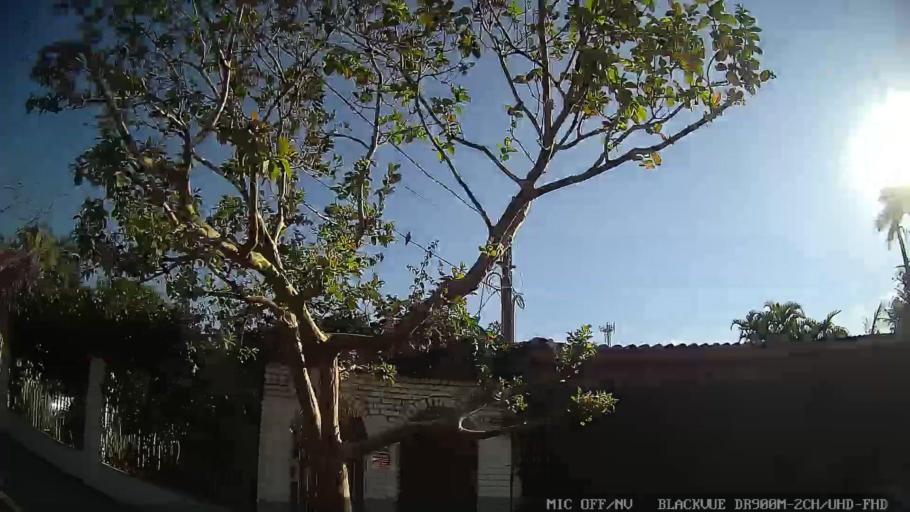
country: BR
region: Sao Paulo
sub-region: Guaruja
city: Guaruja
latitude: -24.0151
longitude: -46.2852
